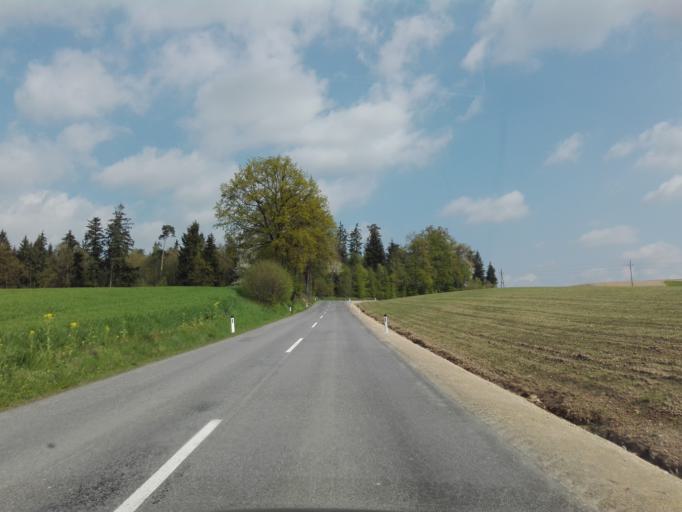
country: AT
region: Upper Austria
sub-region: Politischer Bezirk Perg
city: Perg
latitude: 48.2692
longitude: 14.6527
